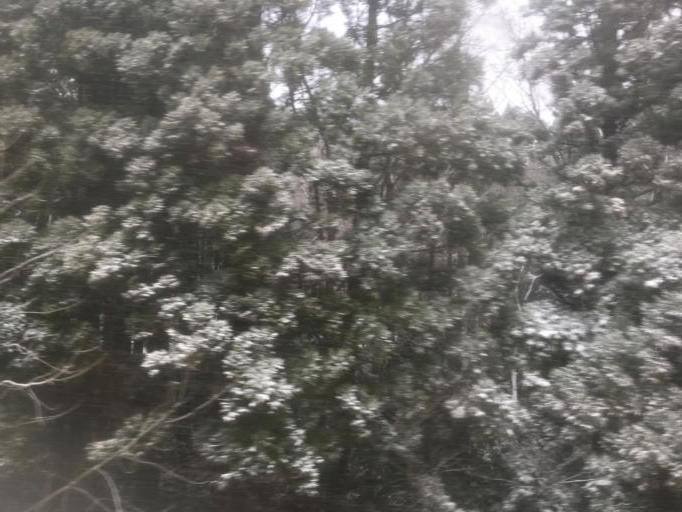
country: JP
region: Aomori
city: Goshogawara
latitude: 41.1164
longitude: 140.5256
